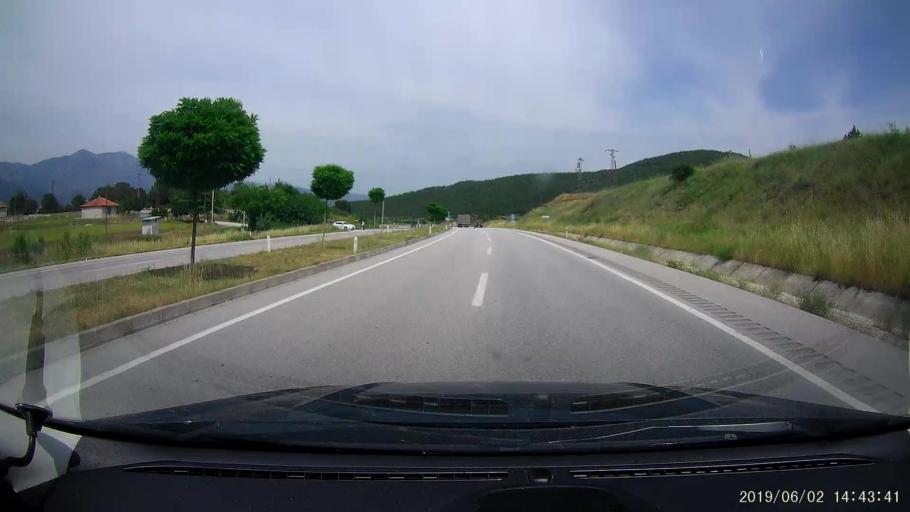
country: TR
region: Corum
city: Hacihamza
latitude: 41.0975
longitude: 34.3942
